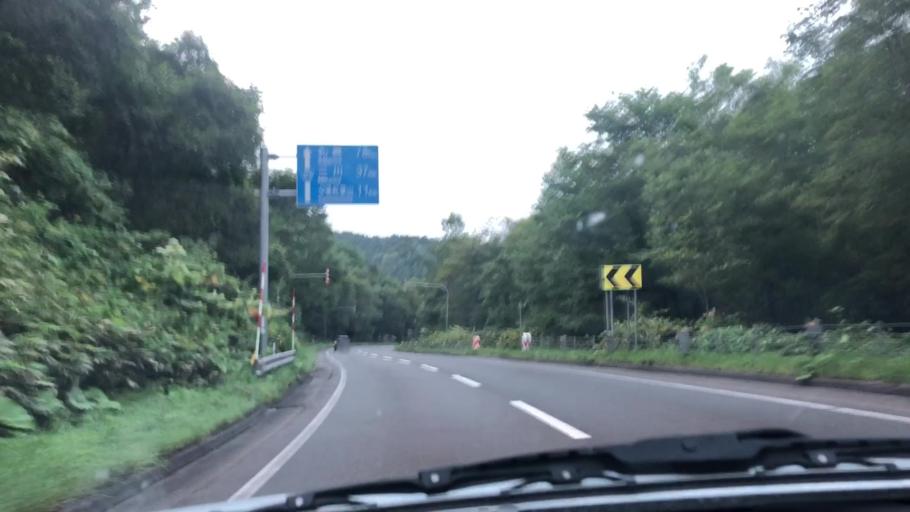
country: JP
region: Hokkaido
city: Chitose
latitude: 42.8893
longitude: 142.1228
